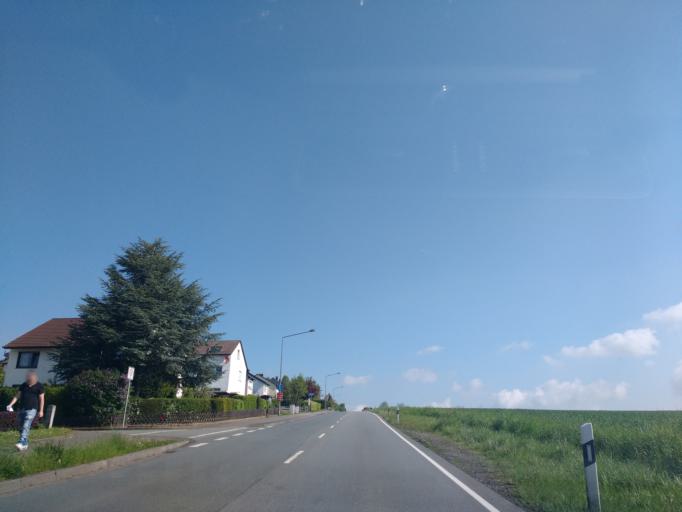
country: DE
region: North Rhine-Westphalia
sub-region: Regierungsbezirk Detmold
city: Detmold
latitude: 51.9172
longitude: 8.9140
